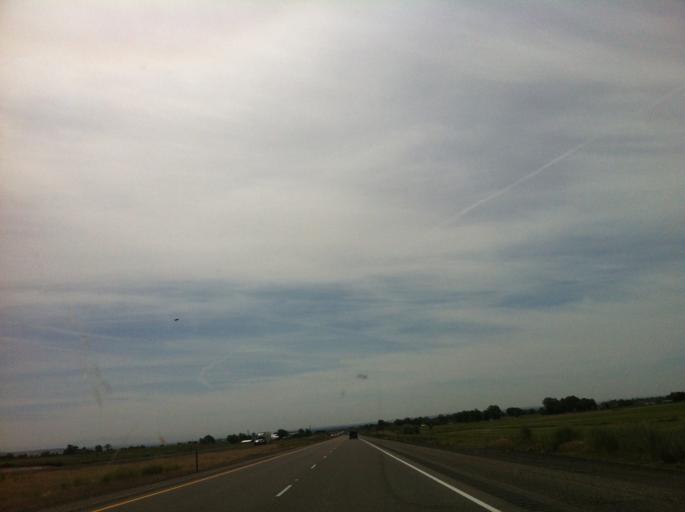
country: US
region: Oregon
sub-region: Malheur County
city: Ontario
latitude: 44.0906
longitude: -117.0271
